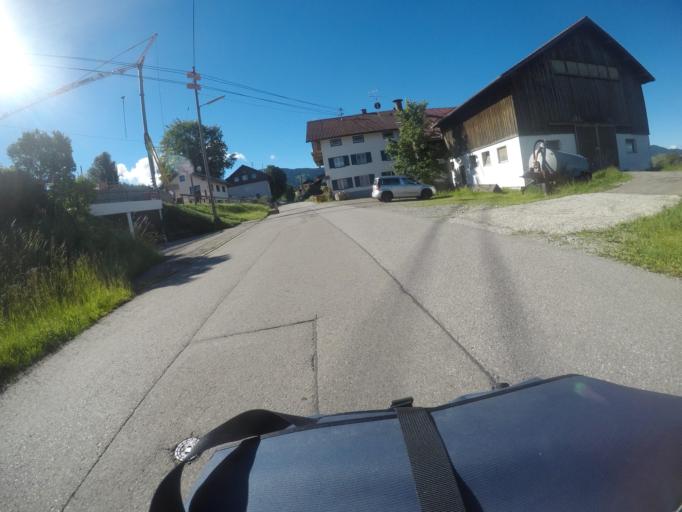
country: DE
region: Bavaria
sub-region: Swabia
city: Oy-Mittelberg
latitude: 47.6305
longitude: 10.4586
